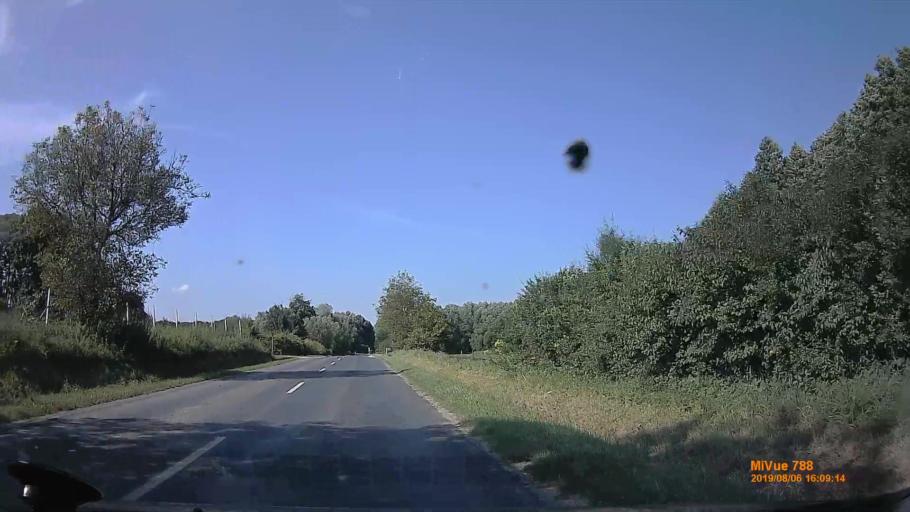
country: HU
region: Zala
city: Murakeresztur
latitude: 46.3336
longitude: 16.9716
